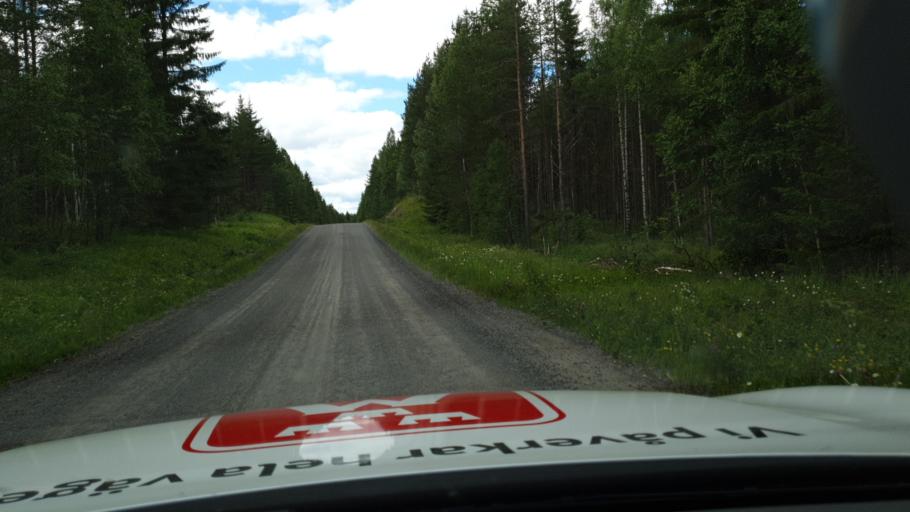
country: SE
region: Jaemtland
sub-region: Braecke Kommun
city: Braecke
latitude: 63.2158
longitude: 15.3596
